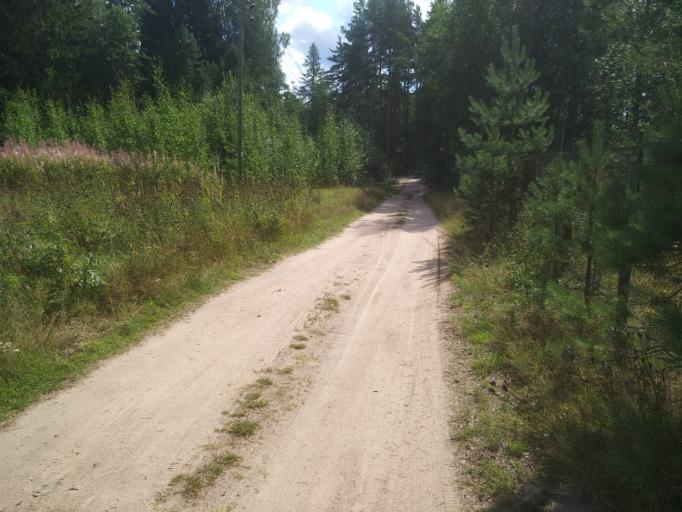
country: RU
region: Leningrad
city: Sapernoye
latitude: 60.6804
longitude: 29.9069
